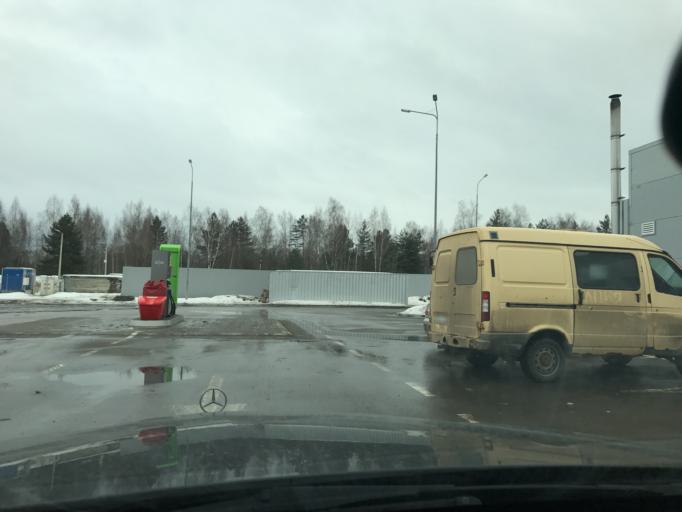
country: RU
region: Vladimir
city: Lakinsk
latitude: 55.9955
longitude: 39.8939
